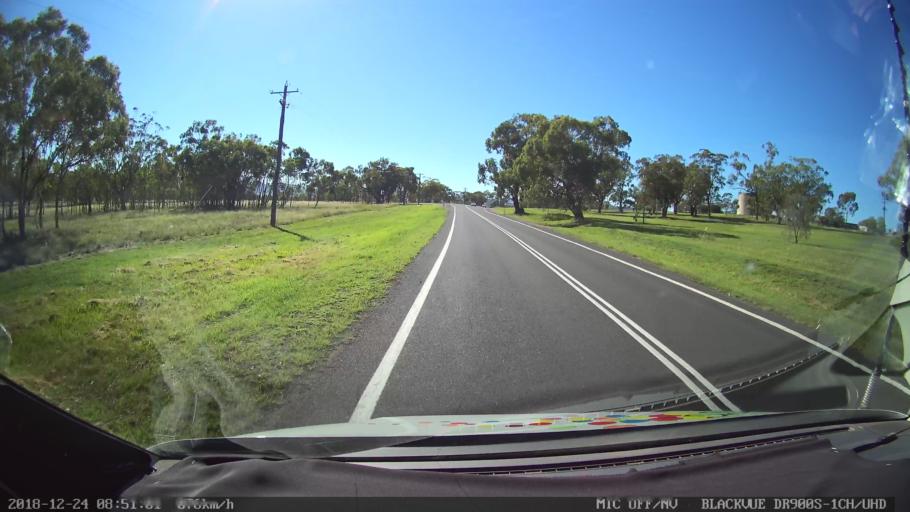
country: AU
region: New South Wales
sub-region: Liverpool Plains
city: Quirindi
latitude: -31.4809
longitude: 150.6706
